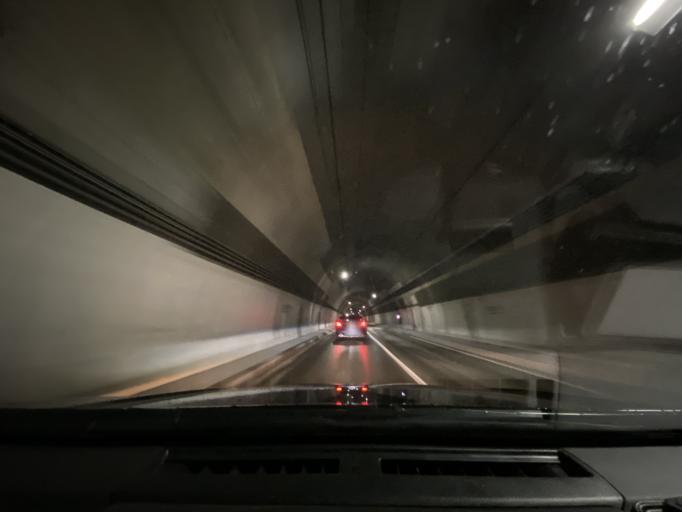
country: JP
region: Hokkaido
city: Ishikari
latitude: 43.4450
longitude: 141.4129
